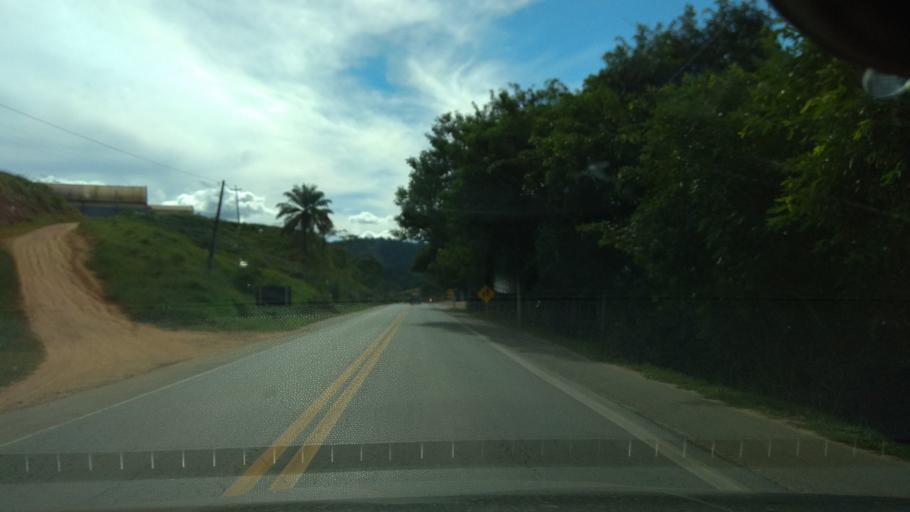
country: BR
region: Bahia
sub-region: Jitauna
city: Jitauna
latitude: -14.0117
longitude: -39.8941
